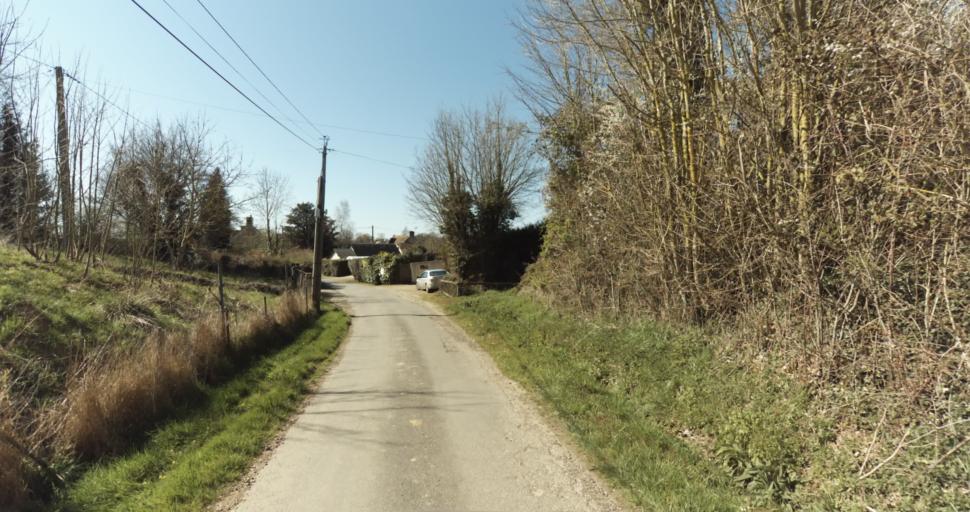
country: FR
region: Lower Normandy
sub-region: Departement du Calvados
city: Saint-Pierre-sur-Dives
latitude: 49.0536
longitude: -0.0221
